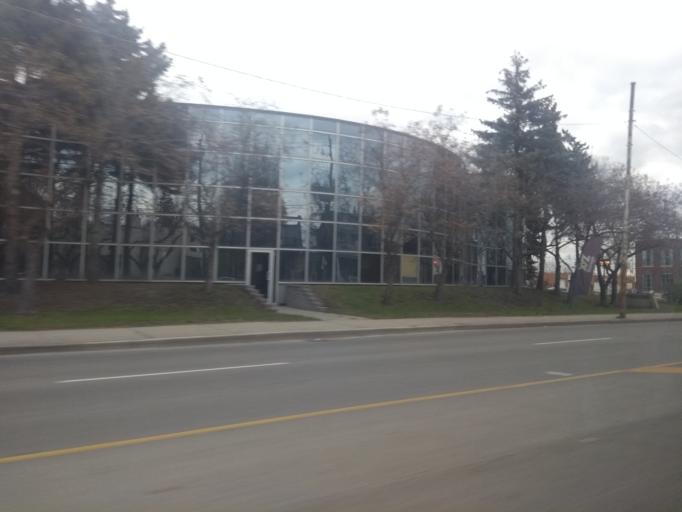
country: CA
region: Ontario
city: Toronto
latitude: 43.6776
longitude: -79.4724
